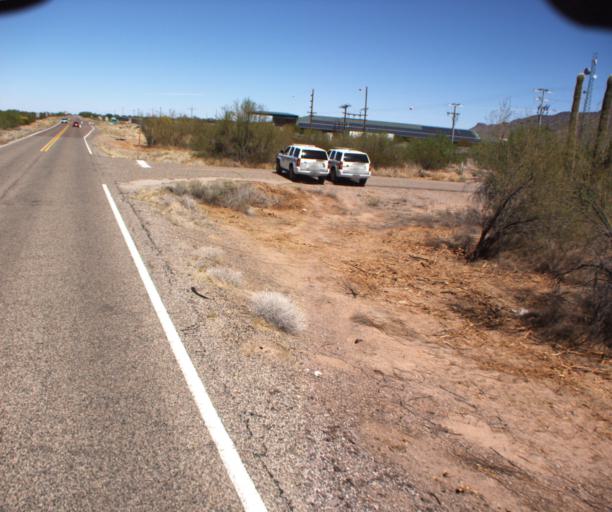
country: US
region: Arizona
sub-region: Pima County
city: Ajo
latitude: 32.2732
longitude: -112.7409
